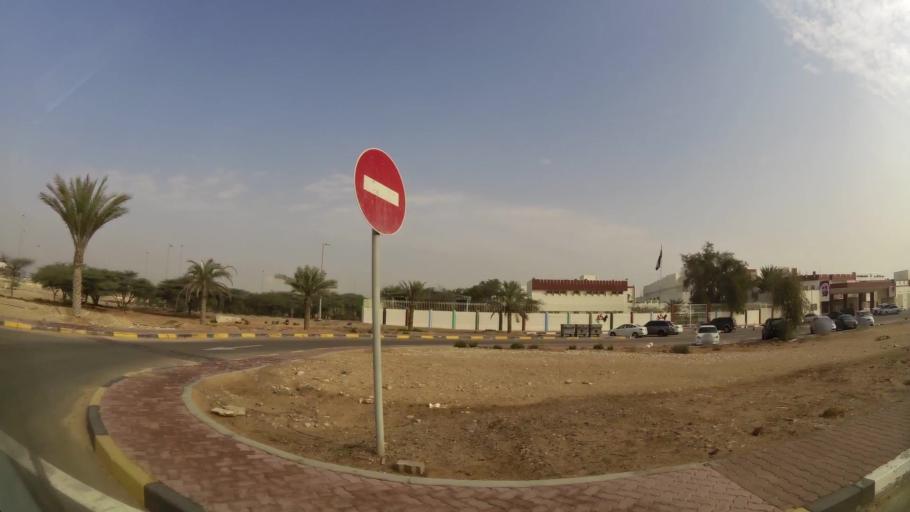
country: AE
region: Abu Dhabi
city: Abu Dhabi
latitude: 24.6808
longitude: 54.7723
